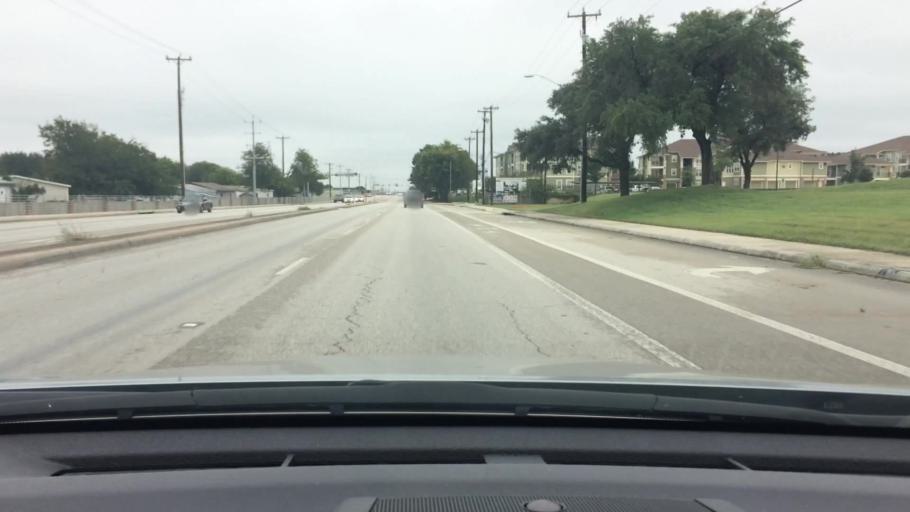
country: US
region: Texas
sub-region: Bexar County
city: Helotes
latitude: 29.5002
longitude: -98.7207
